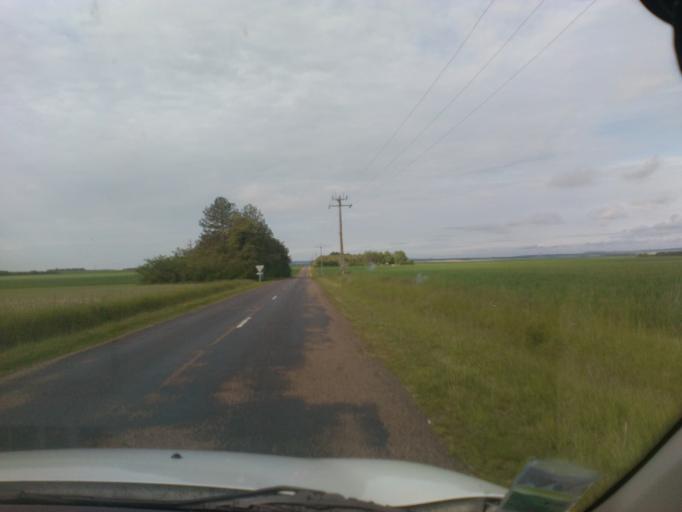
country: FR
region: Champagne-Ardenne
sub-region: Departement de l'Aube
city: Marigny-le-Chatel
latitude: 48.3937
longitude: 3.8138
